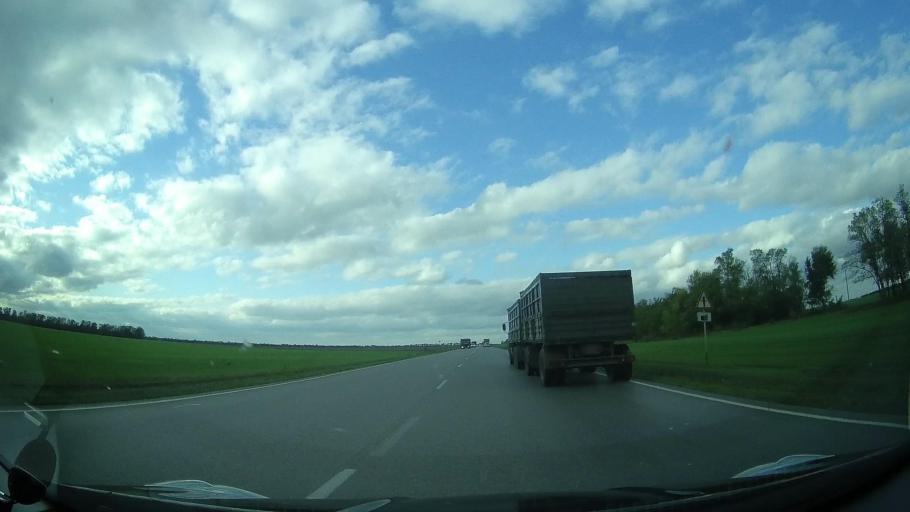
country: RU
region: Rostov
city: Kagal'nitskaya
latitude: 46.9152
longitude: 40.1097
